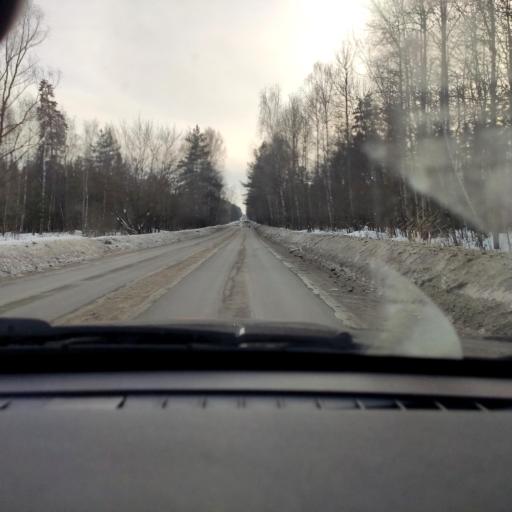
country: RU
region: Samara
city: Pribrezhnyy
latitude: 53.5094
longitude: 49.8503
